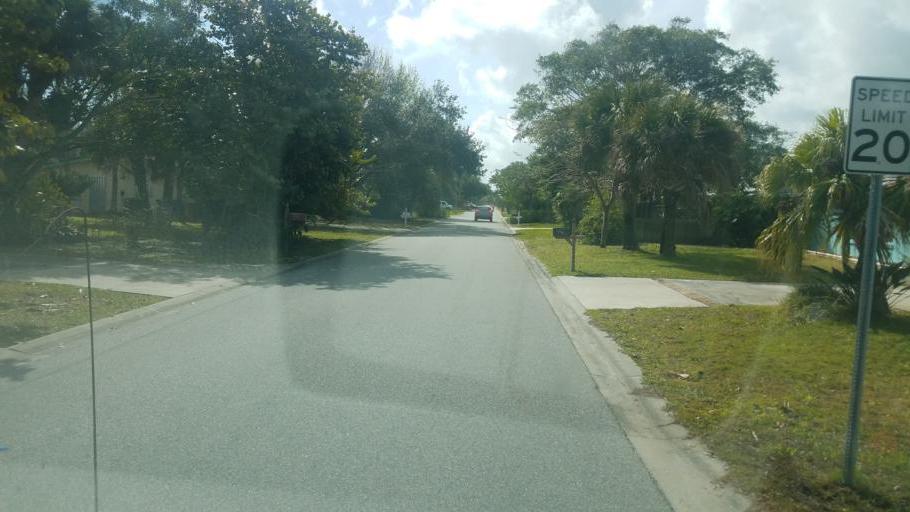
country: US
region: Florida
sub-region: Brevard County
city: Melbourne Beach
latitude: 28.0674
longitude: -80.5631
